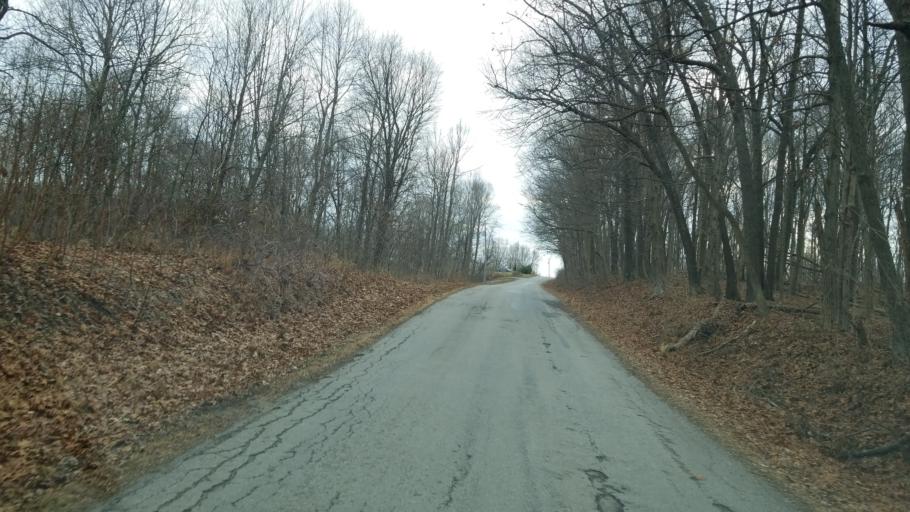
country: US
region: Ohio
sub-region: Highland County
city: Greenfield
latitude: 39.1850
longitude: -83.2663
